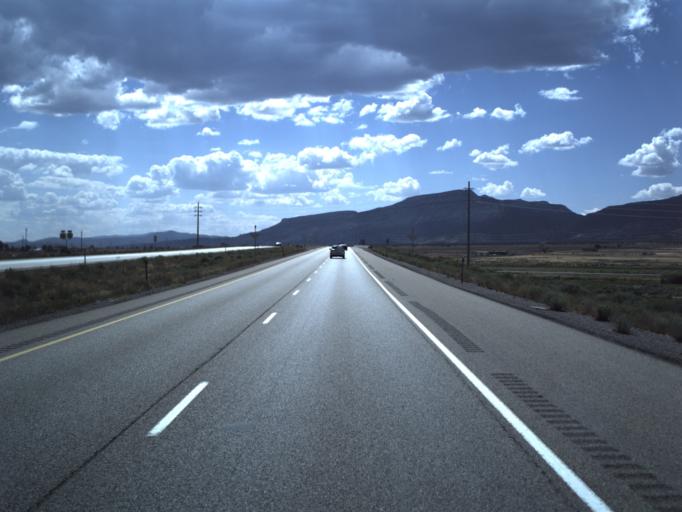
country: US
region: Utah
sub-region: Sevier County
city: Aurora
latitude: 38.8784
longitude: -111.9533
